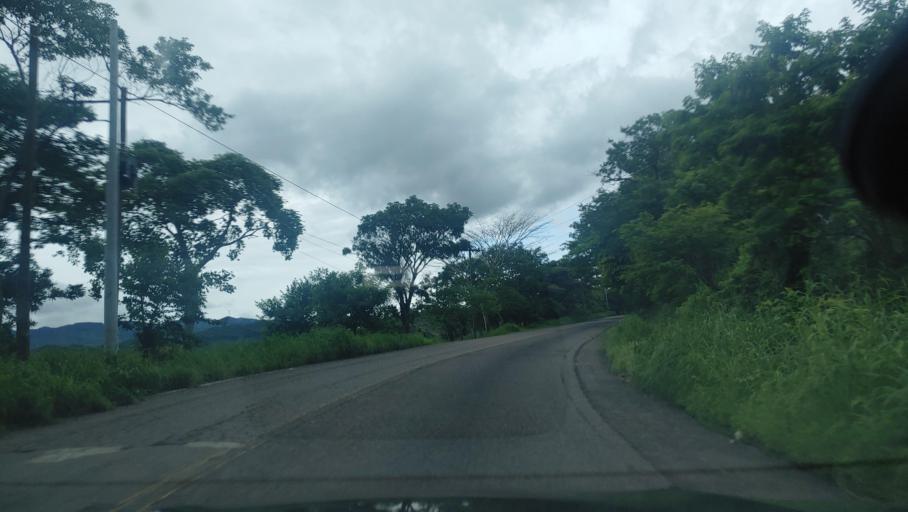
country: HN
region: Choluteca
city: Corpus
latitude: 13.3751
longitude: -87.0459
